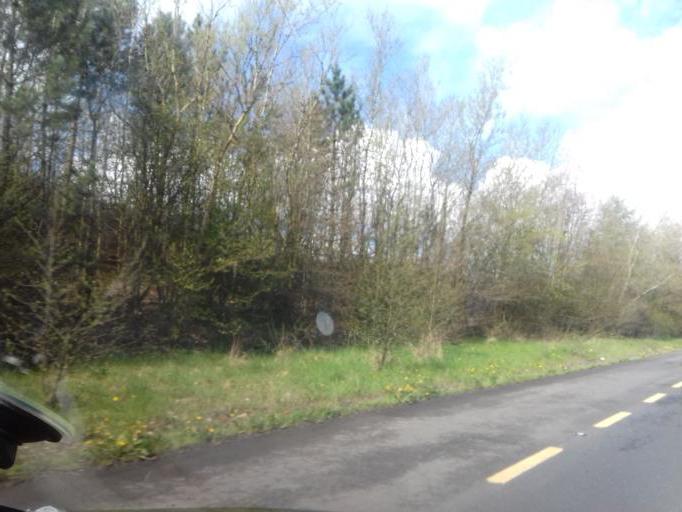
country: IE
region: Ulster
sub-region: An Cabhan
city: Belturbet
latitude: 54.1164
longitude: -7.4771
